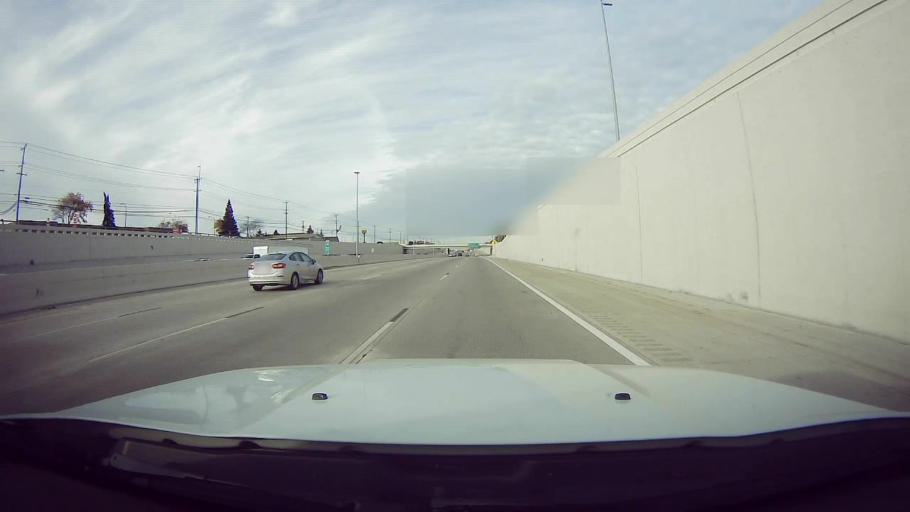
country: US
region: Michigan
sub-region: Wayne County
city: Redford
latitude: 42.3842
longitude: -83.3156
